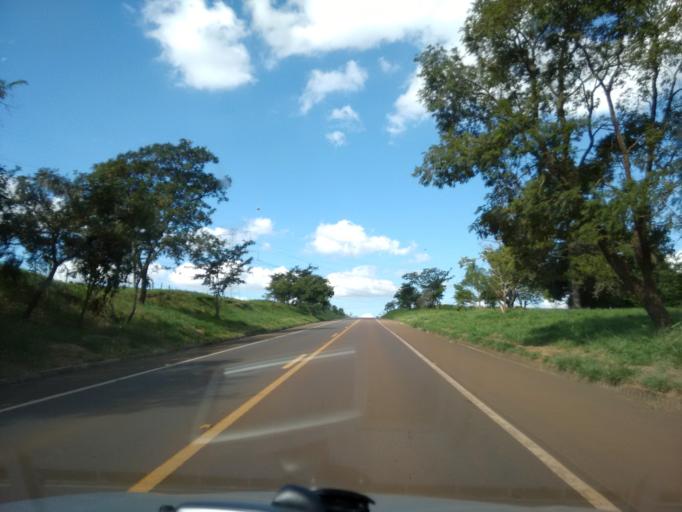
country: BR
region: Sao Paulo
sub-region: Sao Carlos
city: Sao Carlos
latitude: -22.0638
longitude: -47.9369
